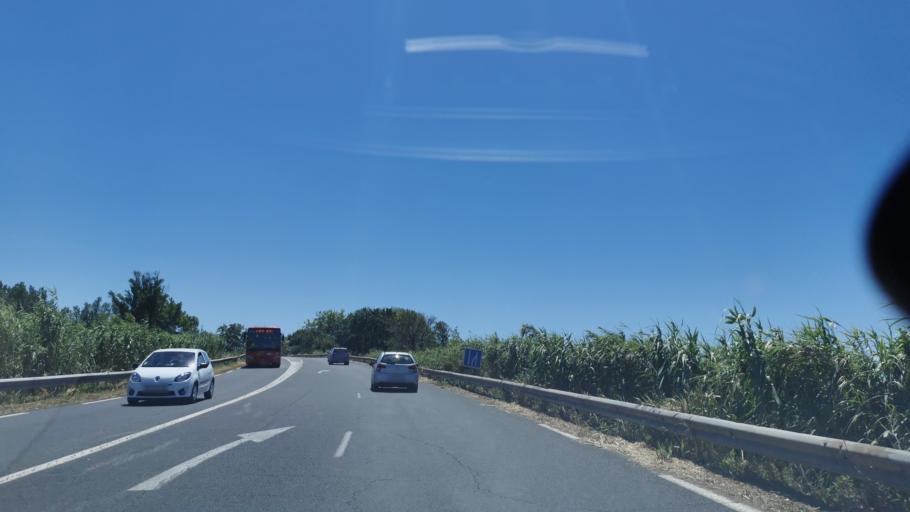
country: FR
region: Languedoc-Roussillon
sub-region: Departement de l'Herault
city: Beziers
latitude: 43.3324
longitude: 3.1947
